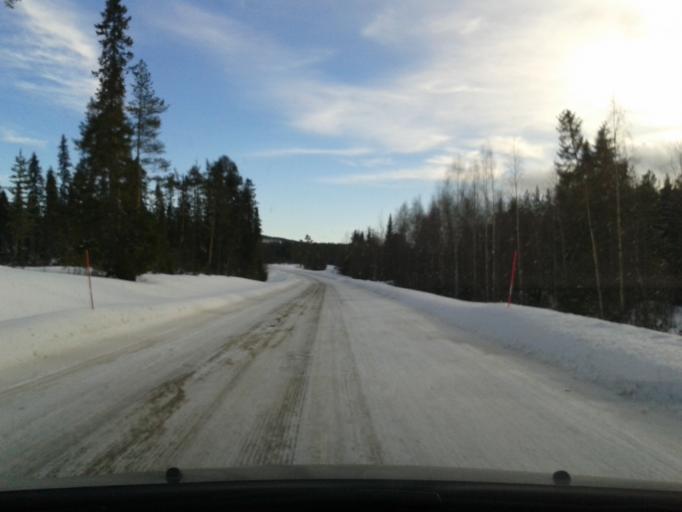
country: SE
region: Vaesterbotten
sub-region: Asele Kommun
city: Asele
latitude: 64.2797
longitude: 17.2662
